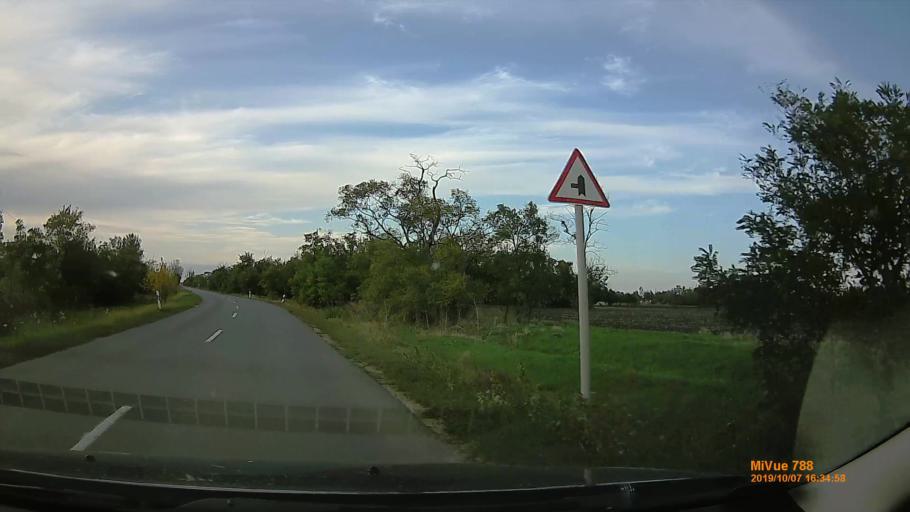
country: HU
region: Bekes
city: Szarvas
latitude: 46.8076
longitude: 20.6172
